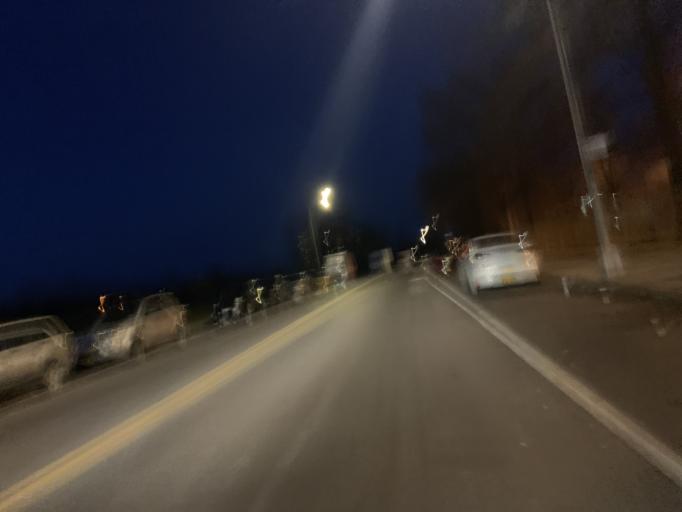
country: US
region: New York
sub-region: New York County
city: Inwood
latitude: 40.8785
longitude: -73.8918
